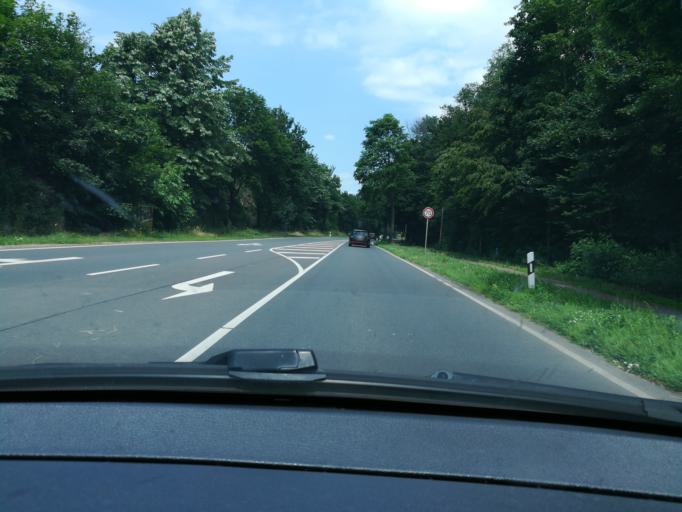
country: DE
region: North Rhine-Westphalia
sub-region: Regierungsbezirk Detmold
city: Minden
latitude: 52.3065
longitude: 8.9636
